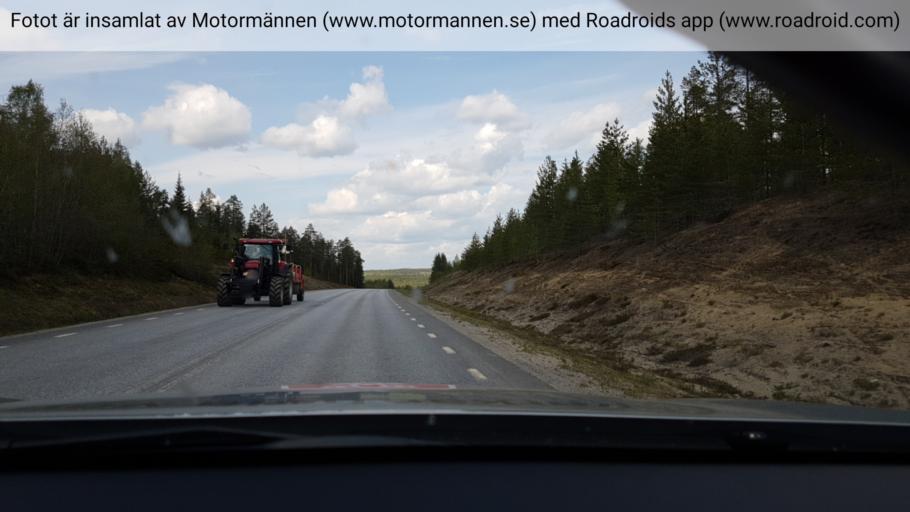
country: SE
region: Vaesterbotten
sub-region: Vannas Kommun
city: Vaennaes
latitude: 64.0315
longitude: 19.6921
